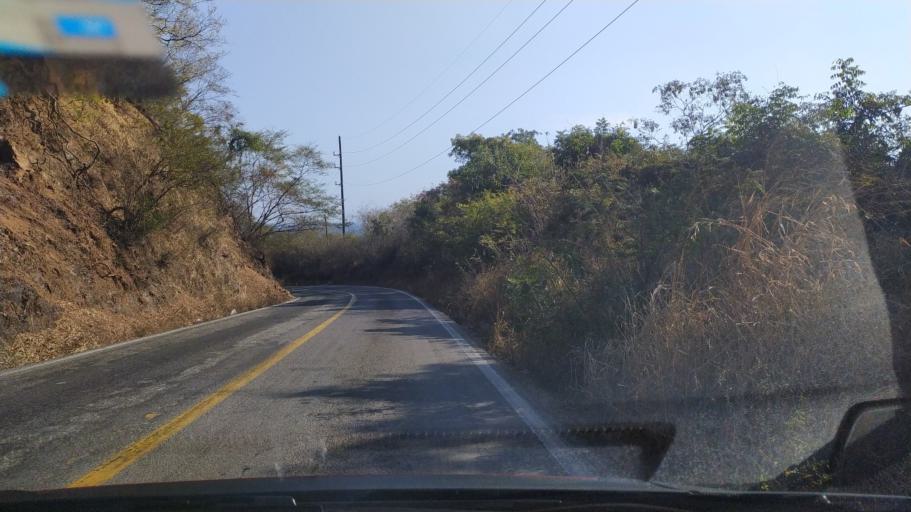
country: MX
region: Michoacan
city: Coahuayana Viejo
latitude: 18.5984
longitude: -103.6795
